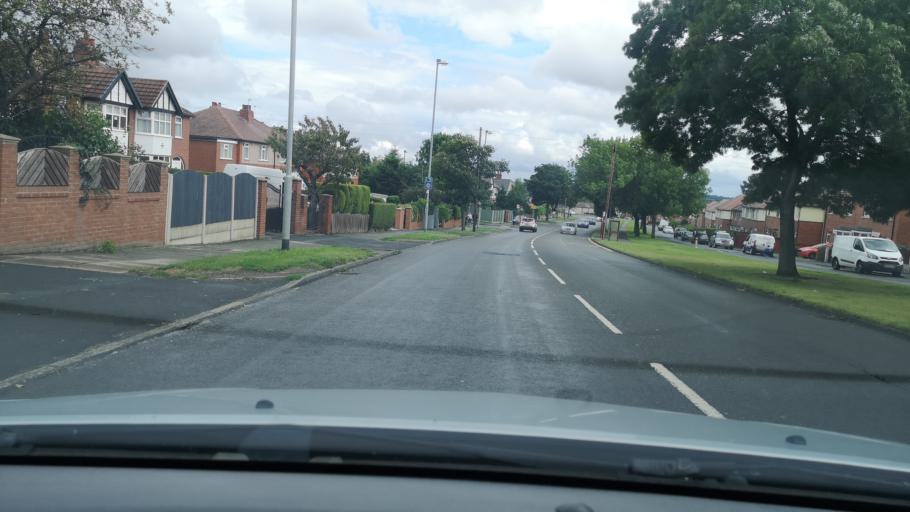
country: GB
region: England
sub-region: City and Borough of Wakefield
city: Horbury
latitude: 53.6792
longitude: -1.5386
